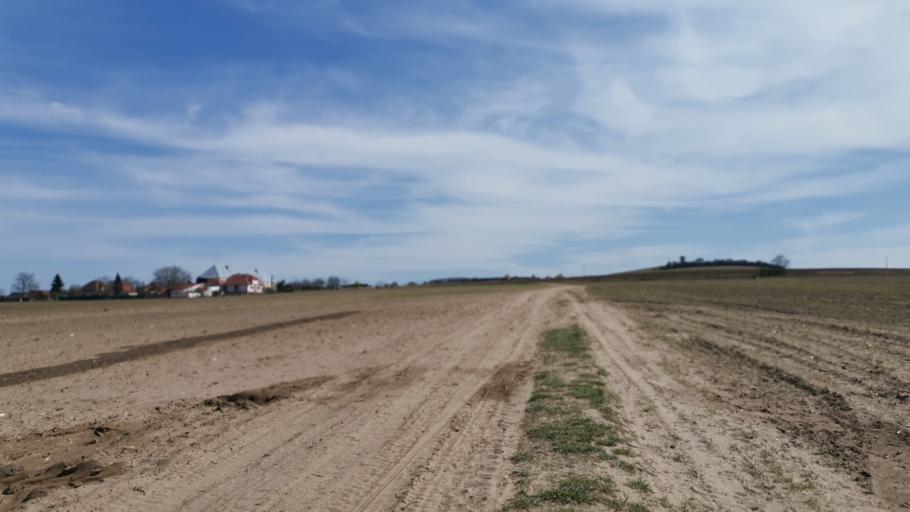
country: SK
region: Trnavsky
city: Gbely
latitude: 48.7114
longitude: 17.1146
